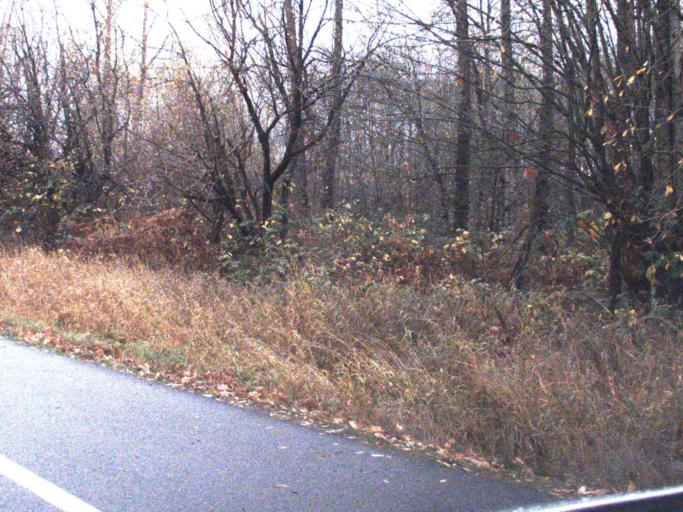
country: US
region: Washington
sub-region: Snohomish County
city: West Lake Stevens
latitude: 47.9989
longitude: -122.1057
